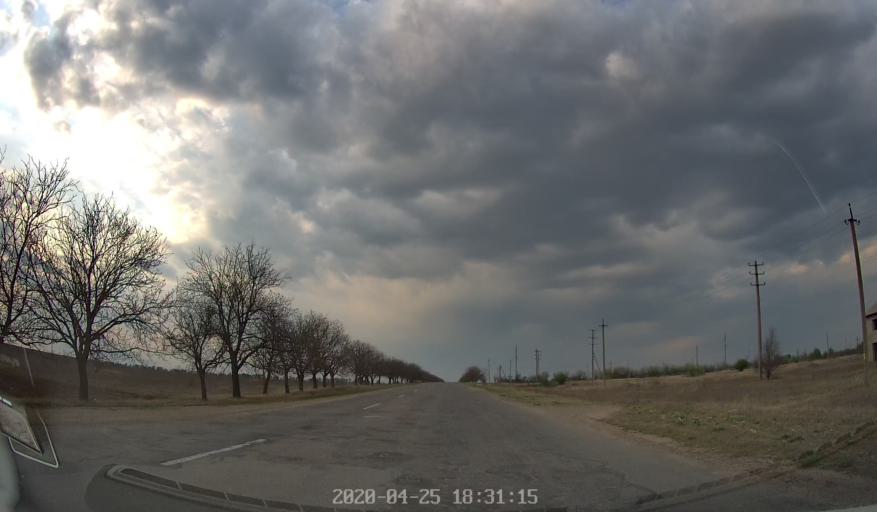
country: MD
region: Criuleni
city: Criuleni
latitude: 47.2153
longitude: 29.1479
